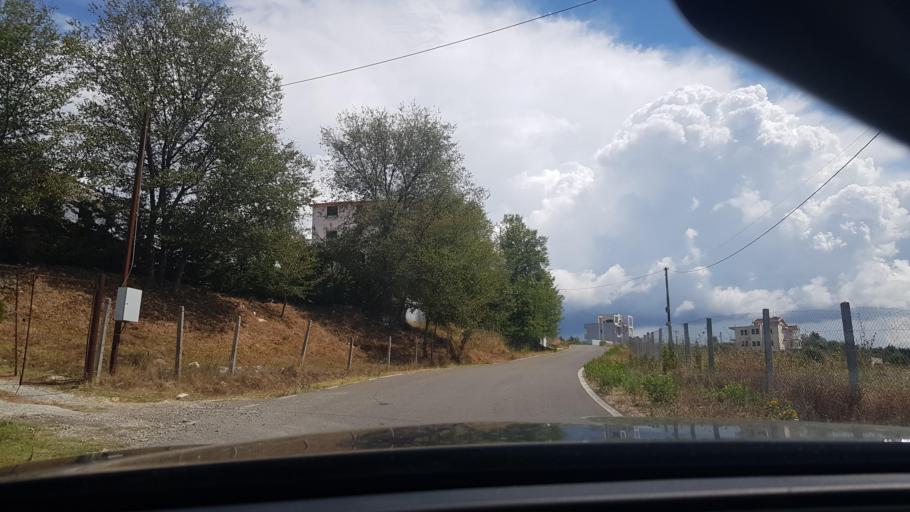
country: AL
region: Durres
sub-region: Rrethi i Durresit
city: Rrashbull
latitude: 41.2945
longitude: 19.5337
